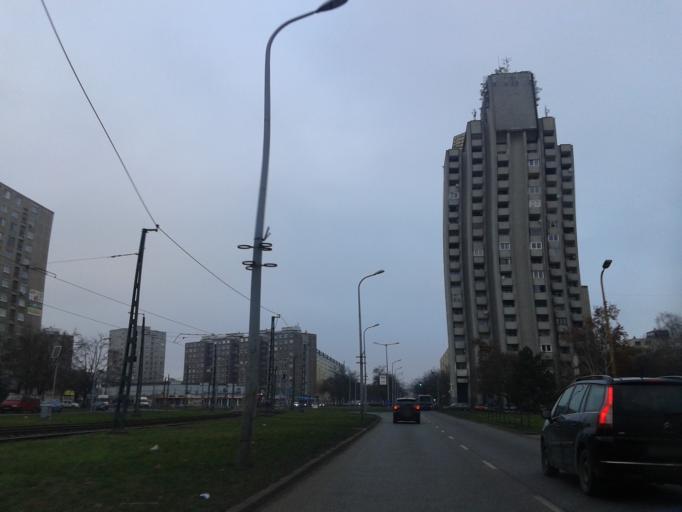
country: HU
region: Budapest
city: Budapest XV. keruelet
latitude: 47.5431
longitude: 19.1402
